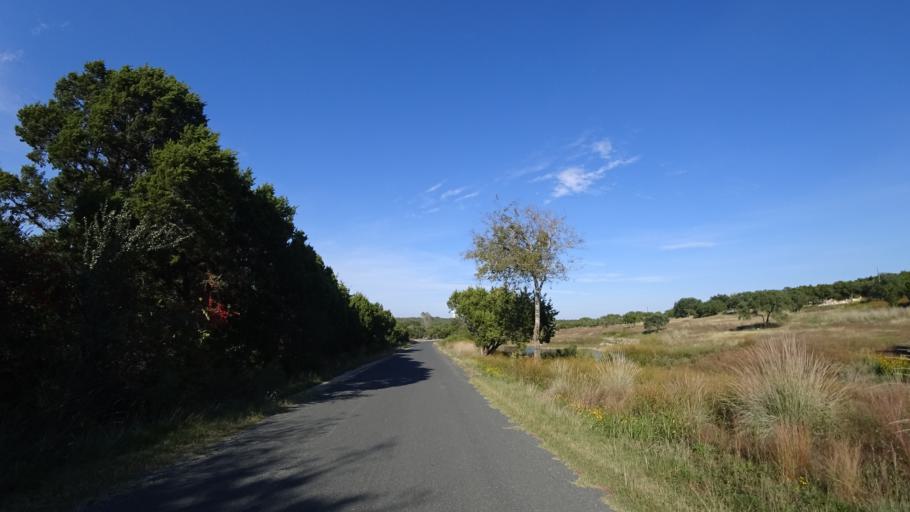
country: US
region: Texas
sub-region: Travis County
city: Bee Cave
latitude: 30.2331
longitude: -97.9320
